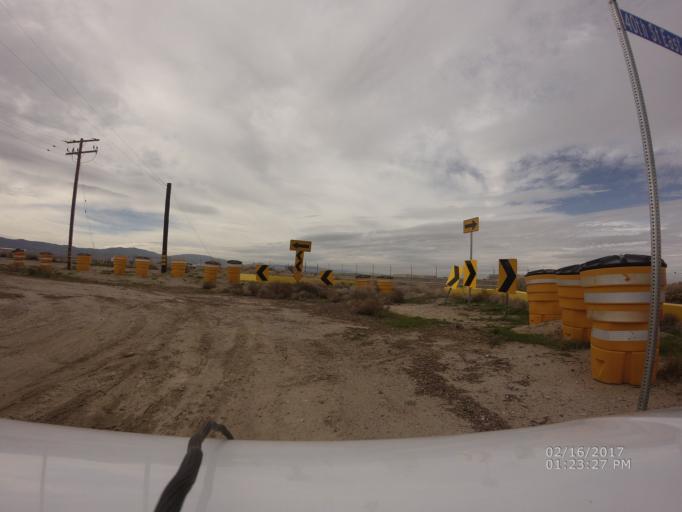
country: US
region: California
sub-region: Los Angeles County
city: Palmdale
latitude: 34.6314
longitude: -118.0586
